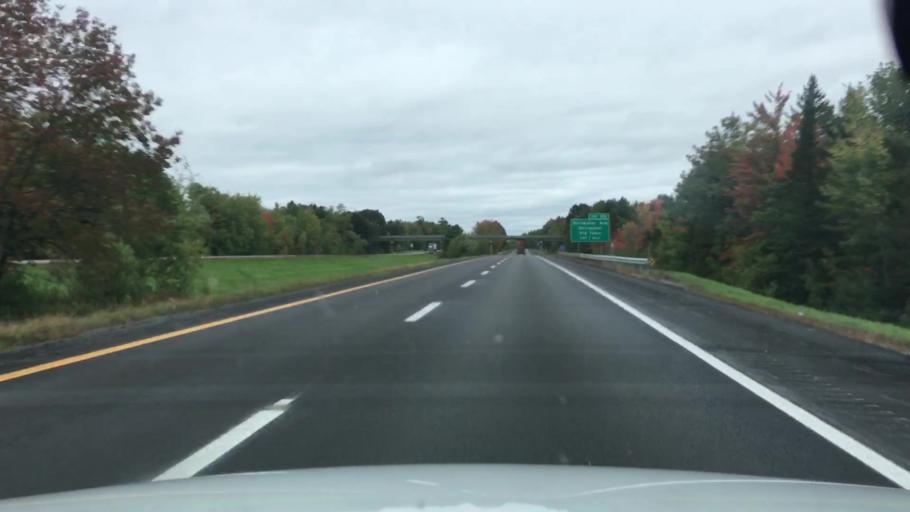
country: US
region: Maine
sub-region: Penobscot County
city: Orono
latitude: 44.8864
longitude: -68.6946
